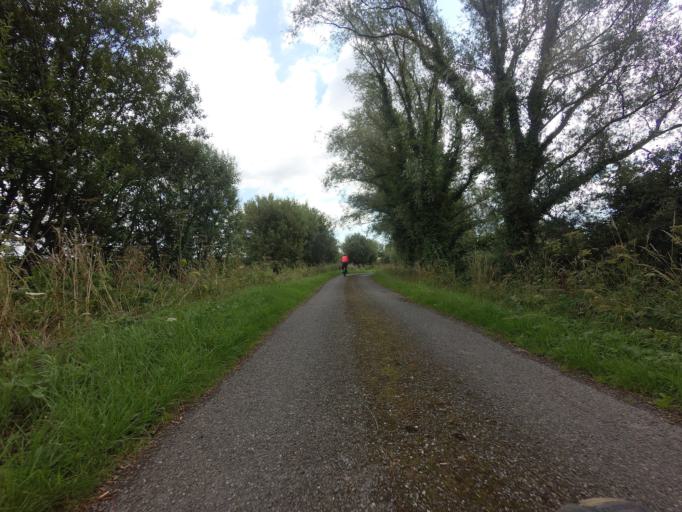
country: GB
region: England
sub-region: Kent
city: Stone
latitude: 51.0548
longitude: 0.7663
